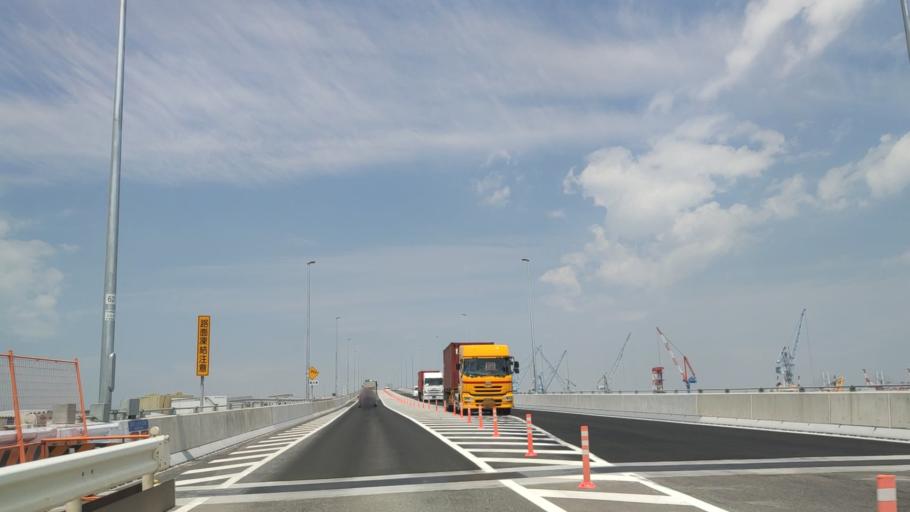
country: JP
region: Kanagawa
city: Yokohama
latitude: 35.4089
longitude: 139.6847
